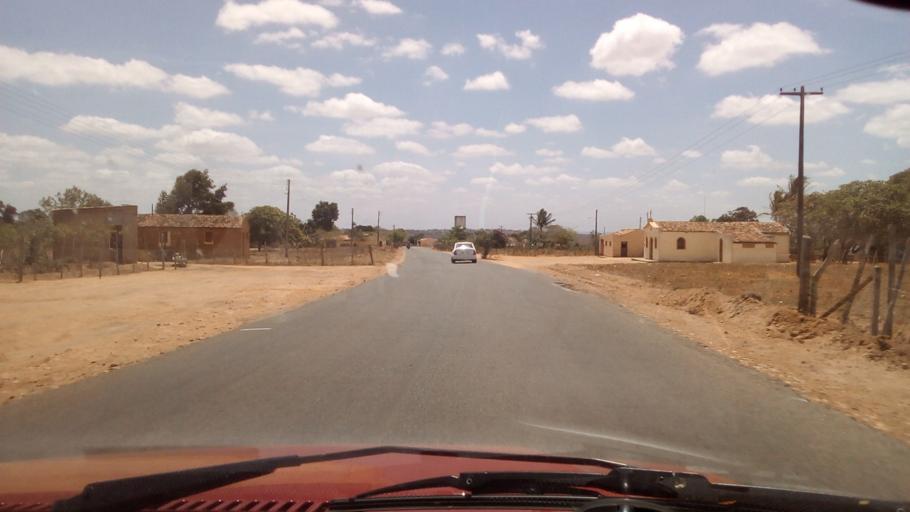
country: BR
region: Paraiba
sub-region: Cacimba De Dentro
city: Cacimba de Dentro
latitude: -6.6058
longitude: -35.8092
